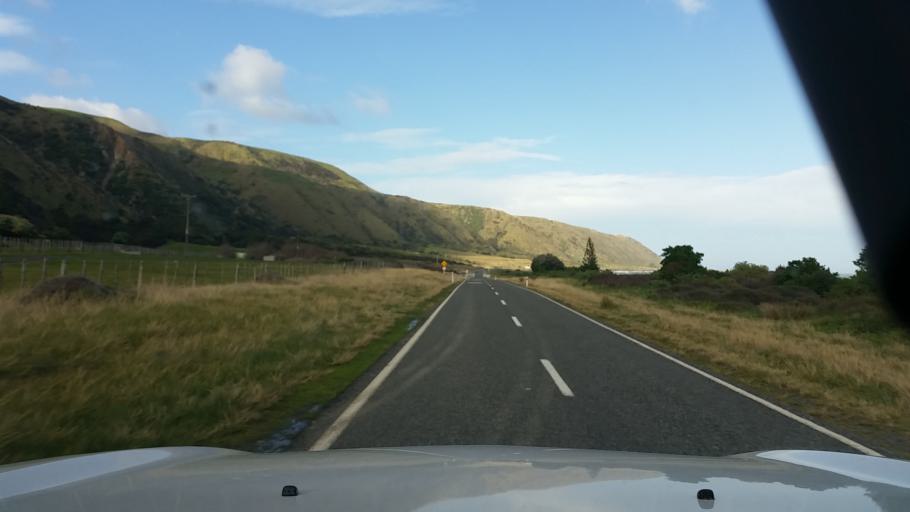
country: NZ
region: Wellington
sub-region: South Wairarapa District
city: Waipawa
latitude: -41.4920
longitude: 175.2091
